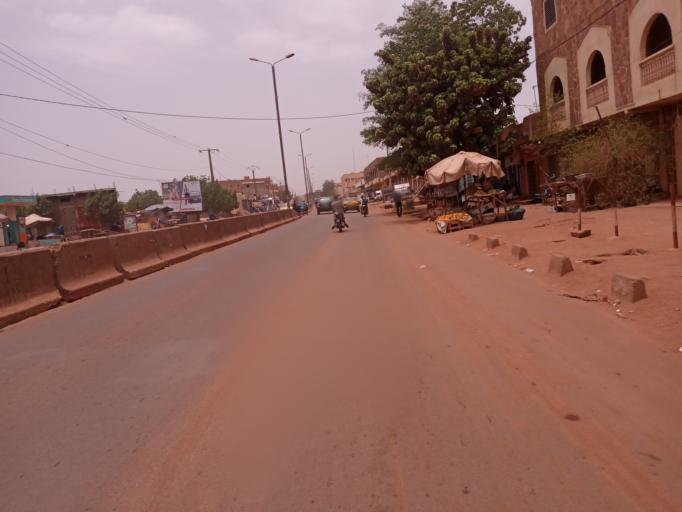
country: ML
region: Bamako
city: Bamako
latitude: 12.5931
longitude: -8.0186
